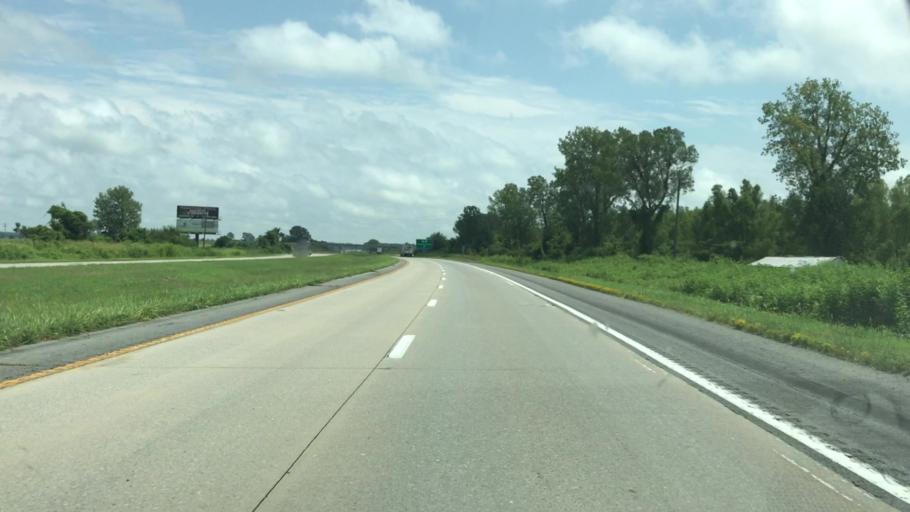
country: US
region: Missouri
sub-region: Pemiscot County
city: Caruthersville
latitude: 36.1552
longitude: -89.6717
